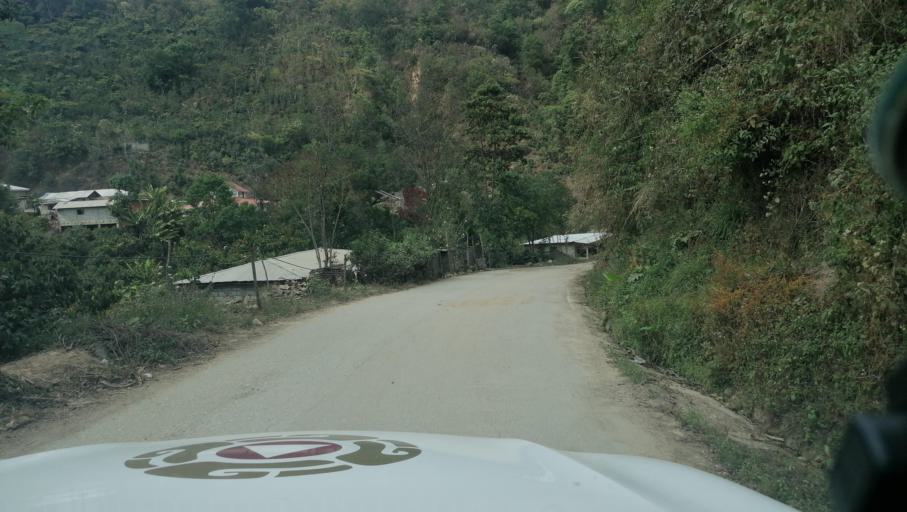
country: GT
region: San Marcos
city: Tacana
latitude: 15.2105
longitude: -92.1946
